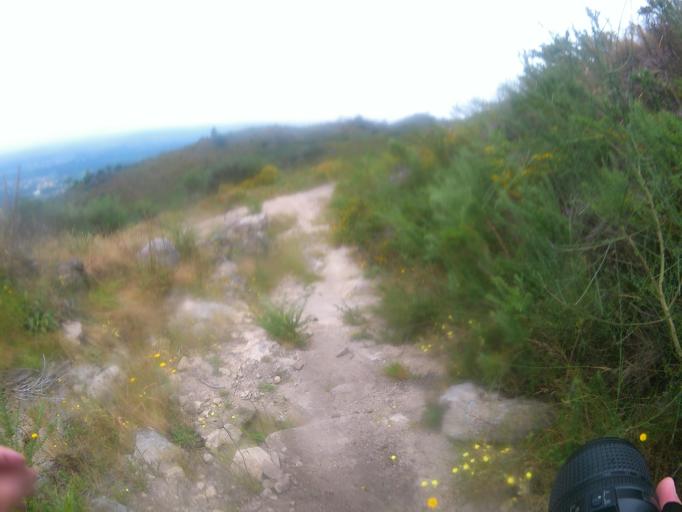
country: PT
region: Viana do Castelo
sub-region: Ponte de Lima
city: Ponte de Lima
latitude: 41.7152
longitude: -8.6035
